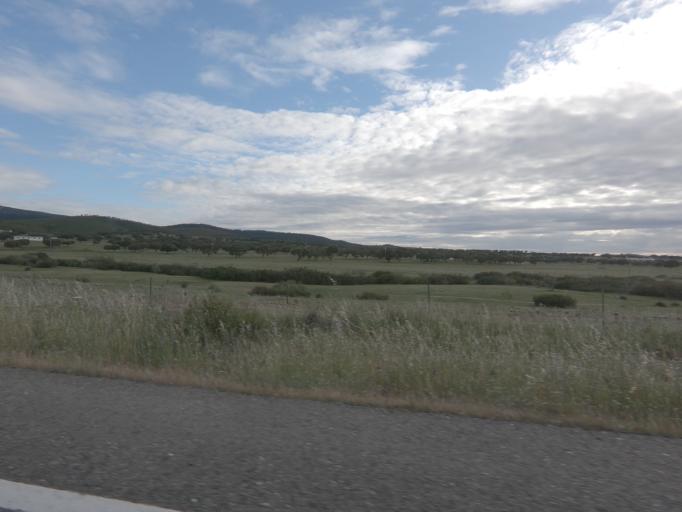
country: ES
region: Extremadura
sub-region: Provincia de Caceres
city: Pedroso de Acim
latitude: 39.8519
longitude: -6.4186
